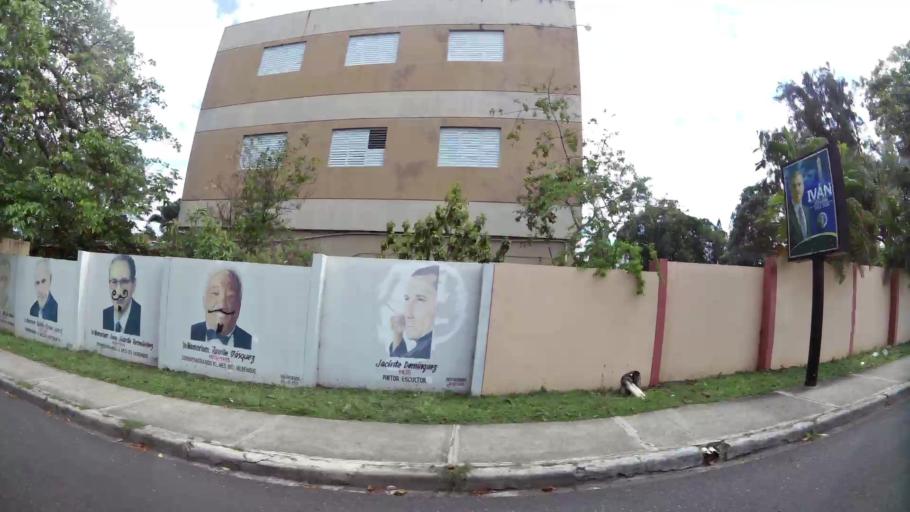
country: DO
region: Santiago
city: Santiago de los Caballeros
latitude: 19.4585
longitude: -70.6892
